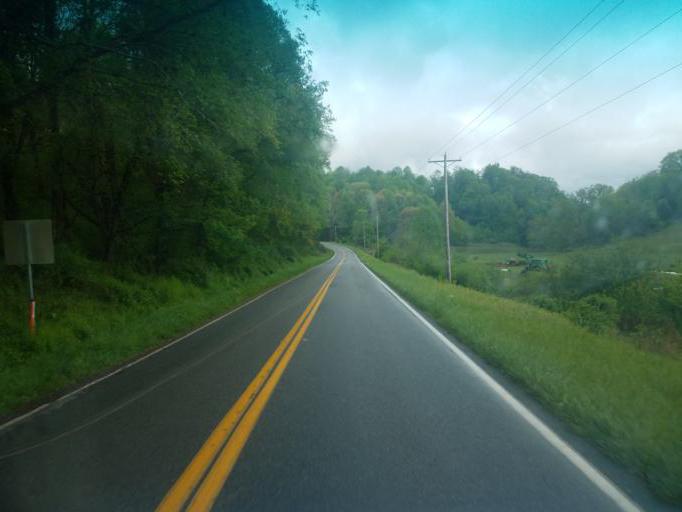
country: US
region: Virginia
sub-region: Washington County
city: Emory
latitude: 36.6443
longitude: -81.7879
